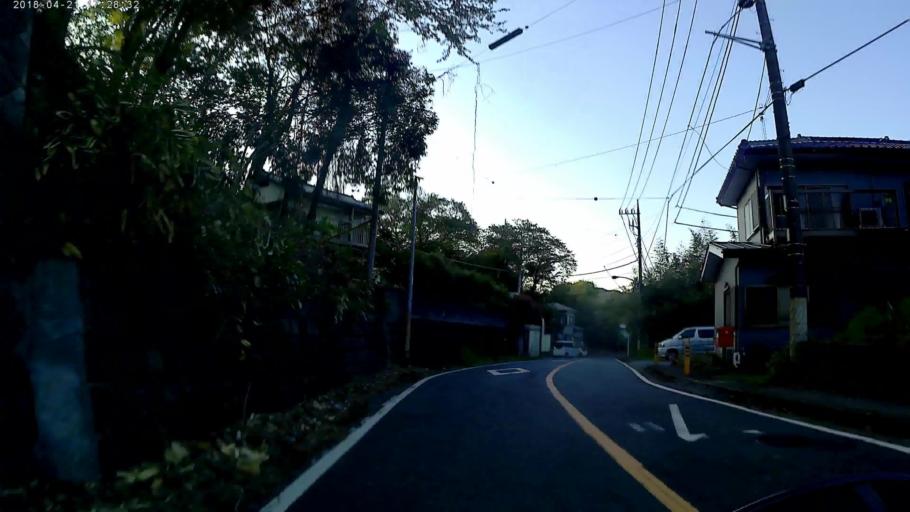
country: JP
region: Kanagawa
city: Atsugi
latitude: 35.4238
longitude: 139.4130
